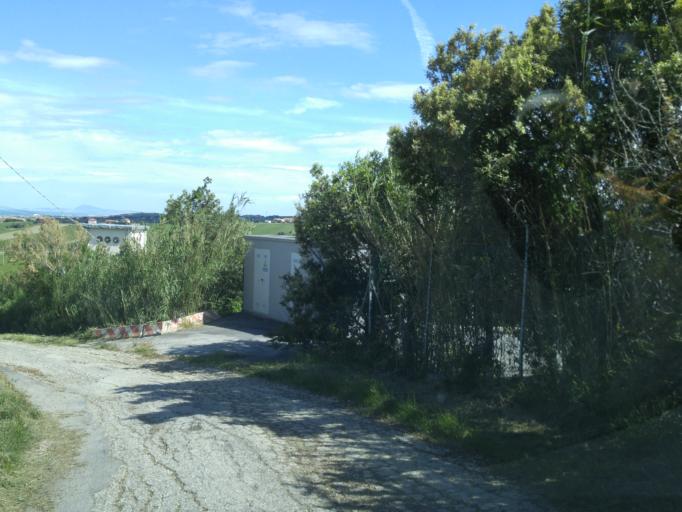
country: IT
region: The Marches
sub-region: Provincia di Pesaro e Urbino
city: San Costanzo
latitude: 43.7897
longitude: 13.0633
